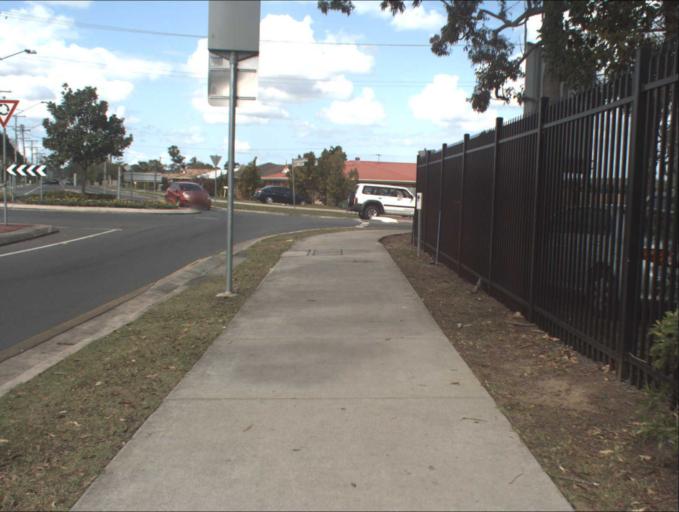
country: AU
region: Queensland
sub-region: Logan
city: Waterford West
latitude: -27.6849
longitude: 153.1123
